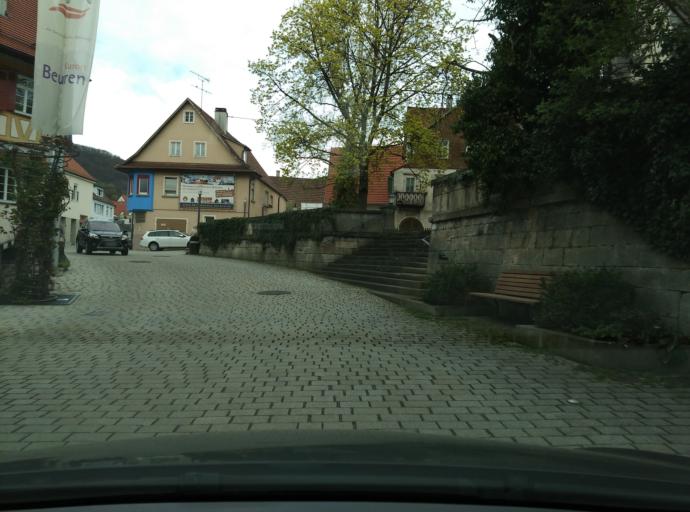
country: DE
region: Baden-Wuerttemberg
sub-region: Regierungsbezirk Stuttgart
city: Beuren
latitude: 48.5695
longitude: 9.4031
